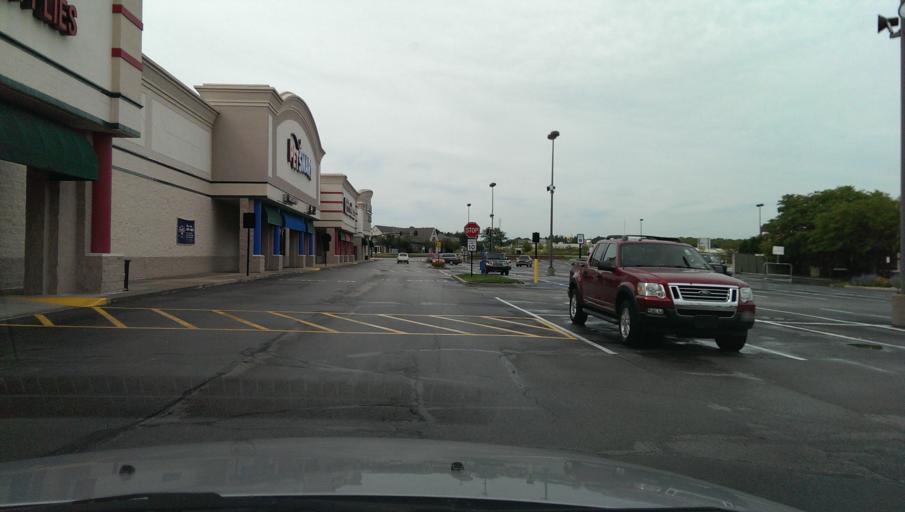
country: US
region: Indiana
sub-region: Hamilton County
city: Carmel
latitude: 40.0020
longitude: -86.1288
